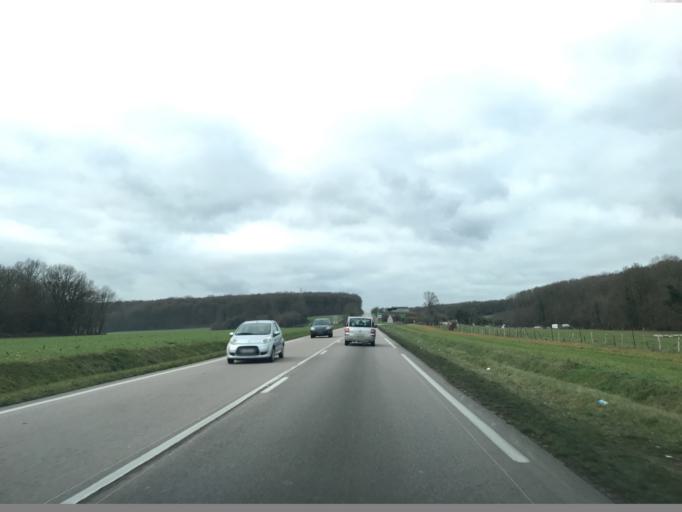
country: FR
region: Haute-Normandie
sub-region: Departement de l'Eure
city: Fleury-sur-Andelle
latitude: 49.3662
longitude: 1.3479
